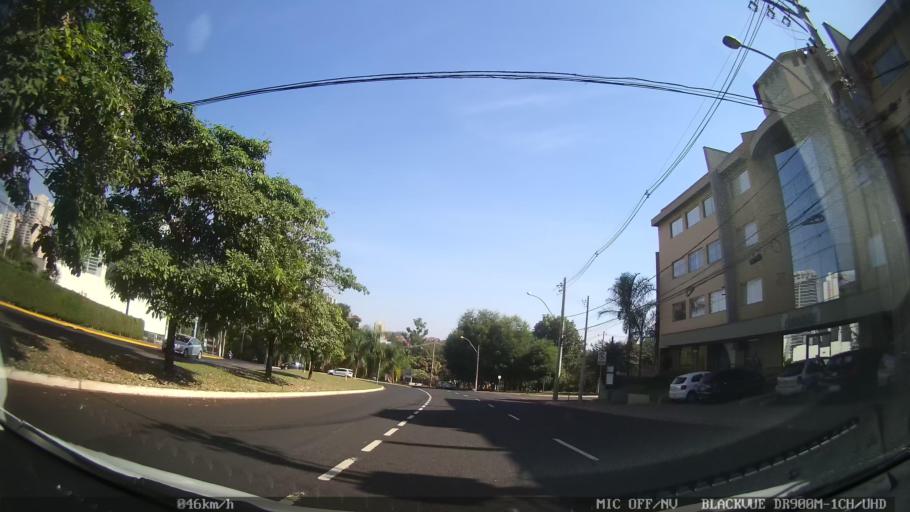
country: BR
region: Sao Paulo
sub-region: Ribeirao Preto
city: Ribeirao Preto
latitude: -21.2113
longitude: -47.8184
